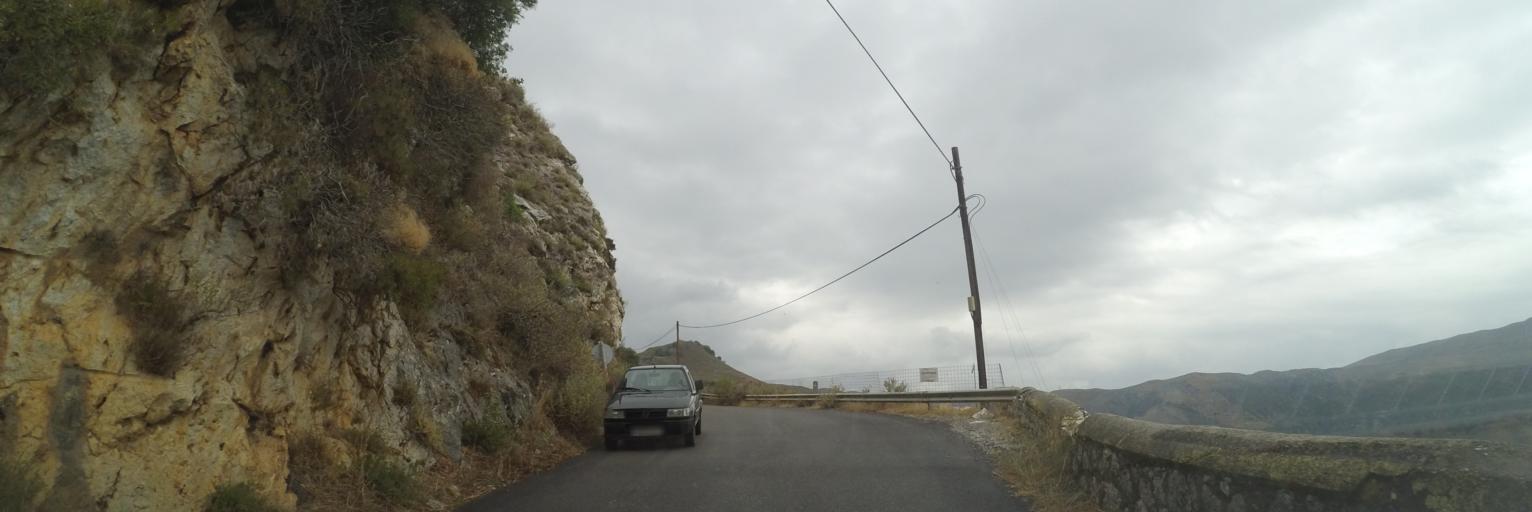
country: GR
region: Crete
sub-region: Nomos Rethymnis
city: Agia Foteini
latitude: 35.2932
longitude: 24.5643
